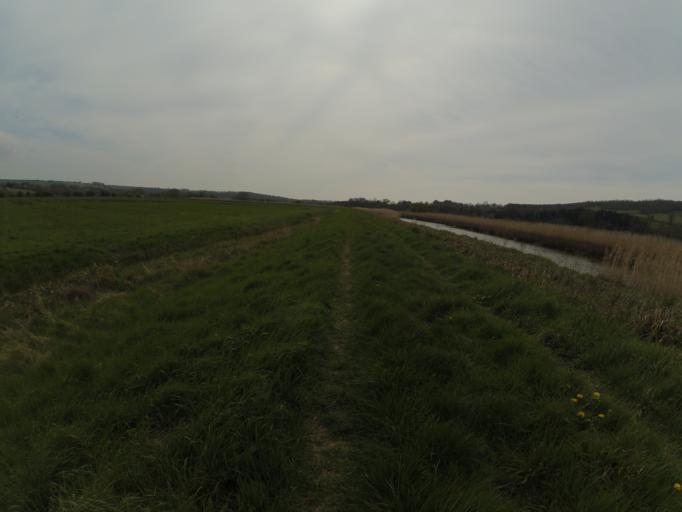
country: GB
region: England
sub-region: West Sussex
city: Arundel
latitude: 50.8762
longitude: -0.5410
